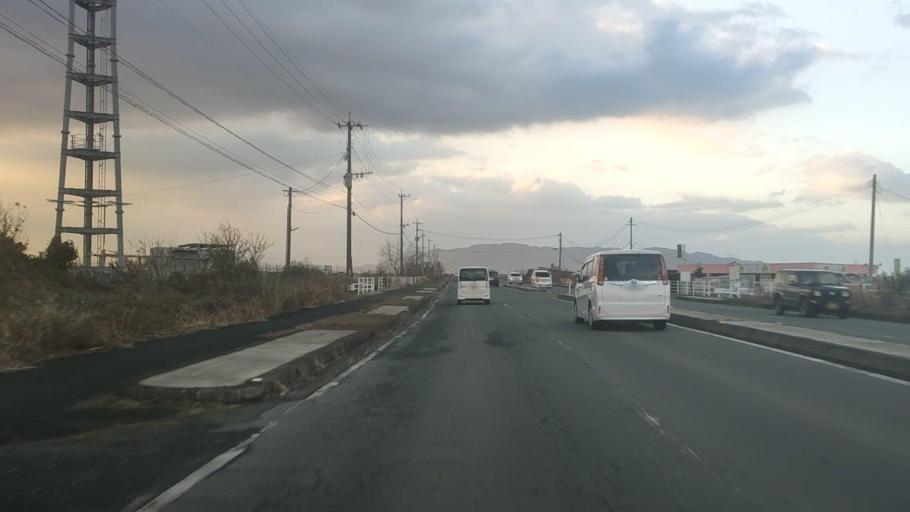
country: JP
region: Kumamoto
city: Kumamoto
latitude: 32.7561
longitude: 130.7062
